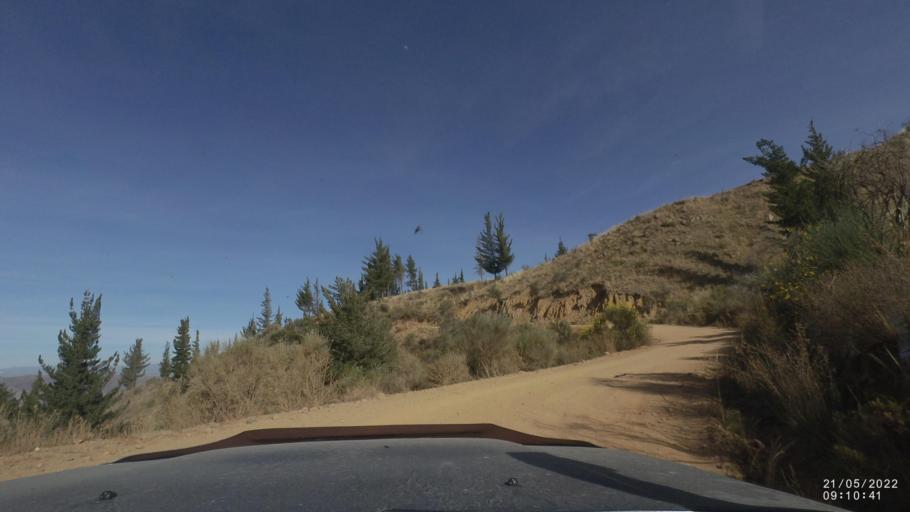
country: BO
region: Cochabamba
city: Cochabamba
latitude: -17.3719
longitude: -66.0216
